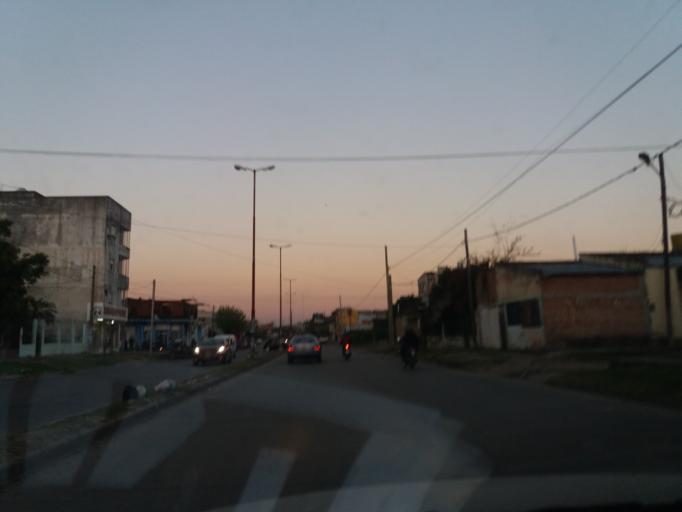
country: AR
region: Corrientes
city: Corrientes
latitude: -27.4855
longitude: -58.8370
